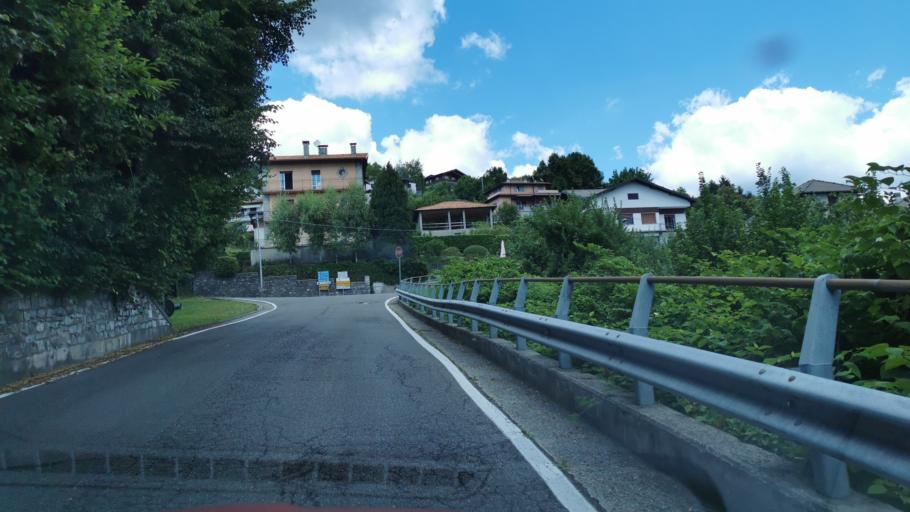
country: IT
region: Lombardy
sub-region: Provincia di Como
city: Pellio Intelvi
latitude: 45.9776
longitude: 9.0638
